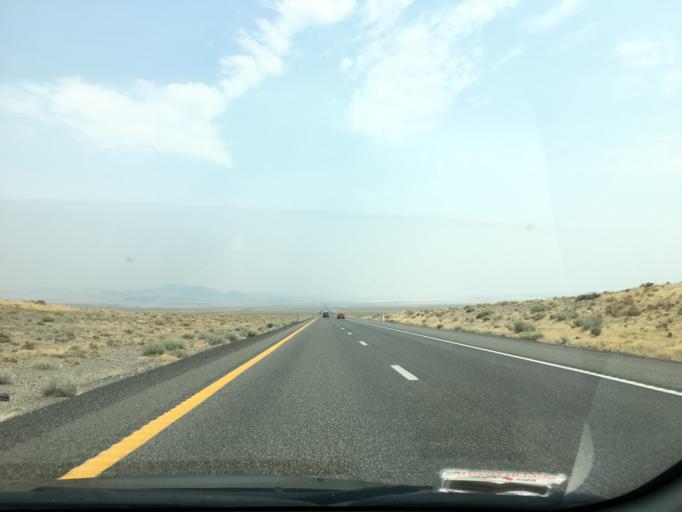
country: US
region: Nevada
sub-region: Churchill County
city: Fallon
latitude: 39.8812
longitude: -118.8704
